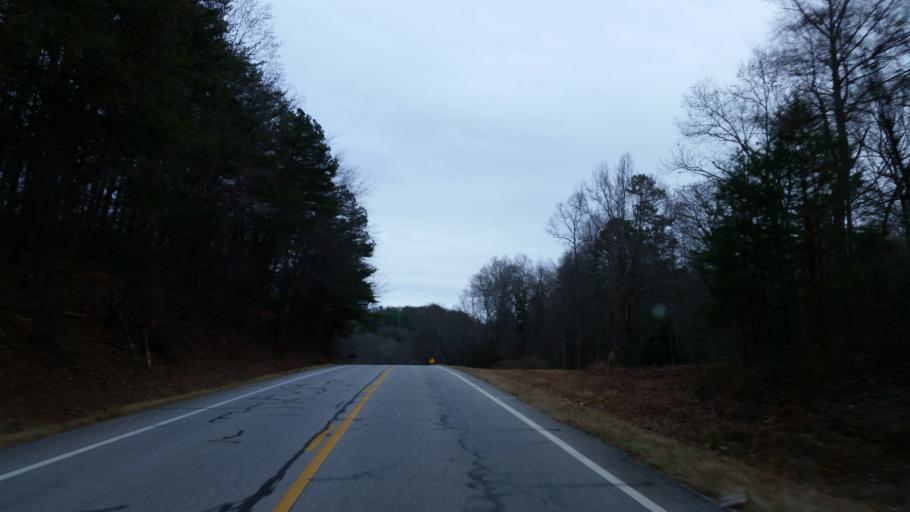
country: US
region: Georgia
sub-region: Dawson County
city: Dawsonville
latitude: 34.5175
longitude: -84.2425
